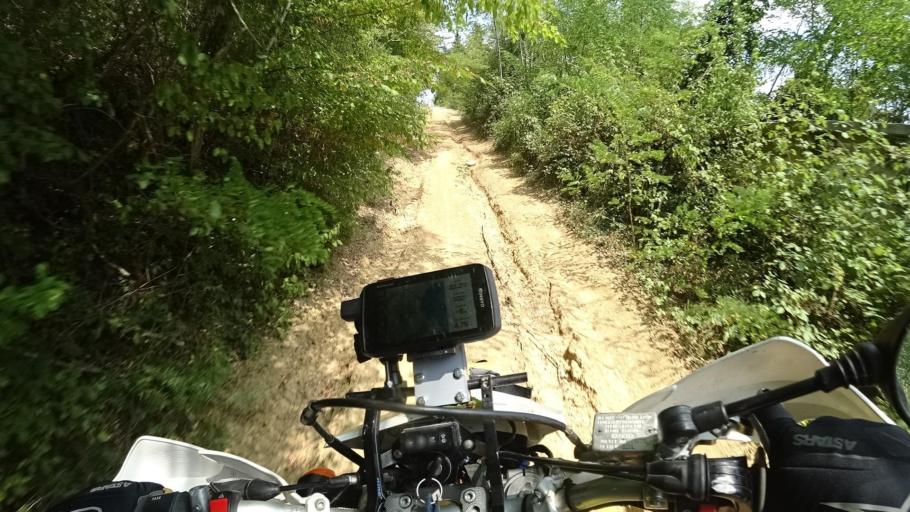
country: HR
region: Istarska
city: Pazin
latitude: 45.3273
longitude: 13.9181
